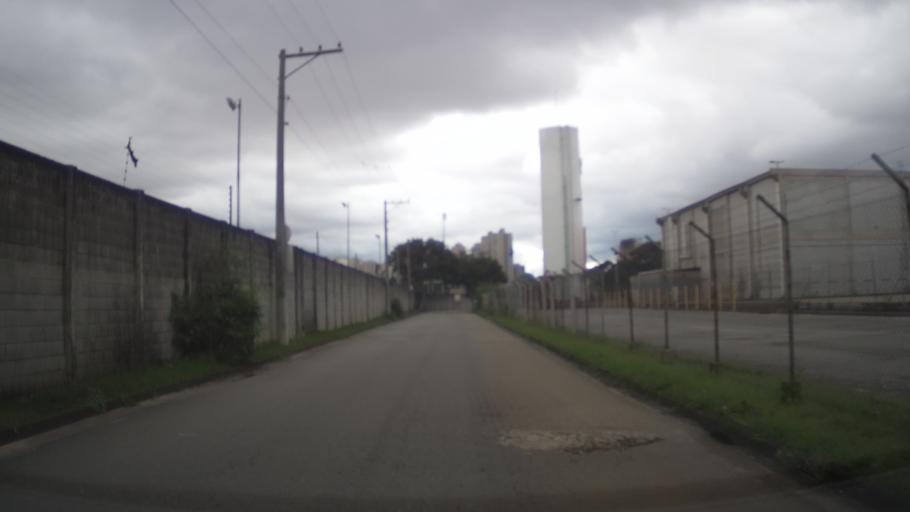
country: BR
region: Sao Paulo
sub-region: Guarulhos
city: Guarulhos
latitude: -23.4812
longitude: -46.5279
